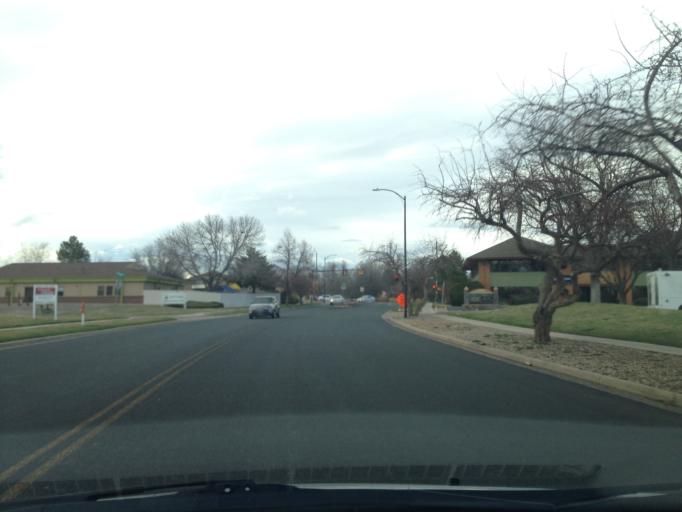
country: US
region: Colorado
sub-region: Boulder County
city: Lafayette
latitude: 39.9856
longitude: -105.1076
